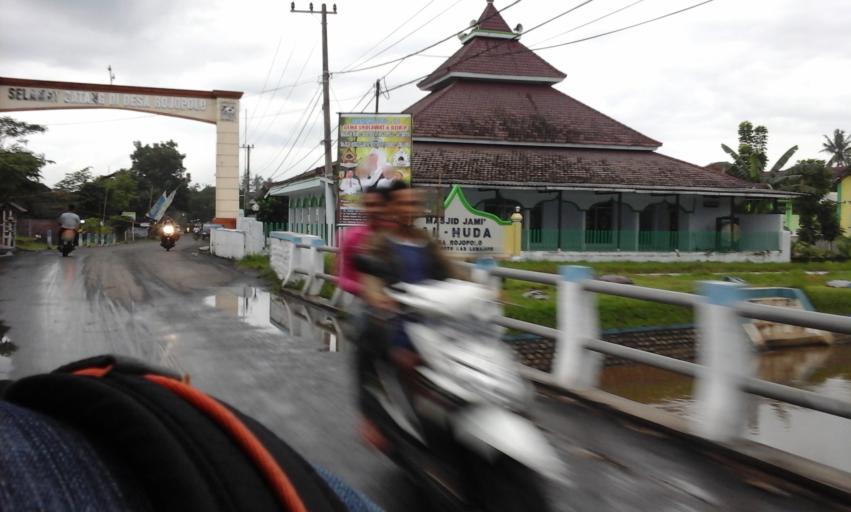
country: ID
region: East Java
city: Sukosari
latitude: -8.1280
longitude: 113.3270
